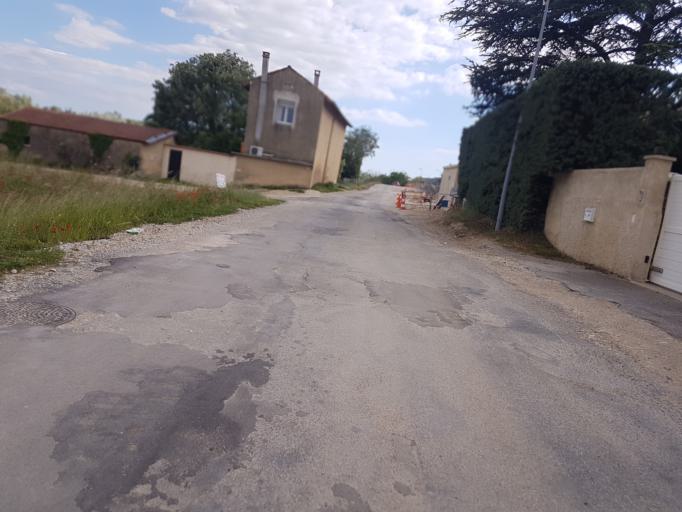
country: FR
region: Rhone-Alpes
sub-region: Departement de l'Ardeche
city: Guilherand-Granges
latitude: 44.9209
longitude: 4.8665
